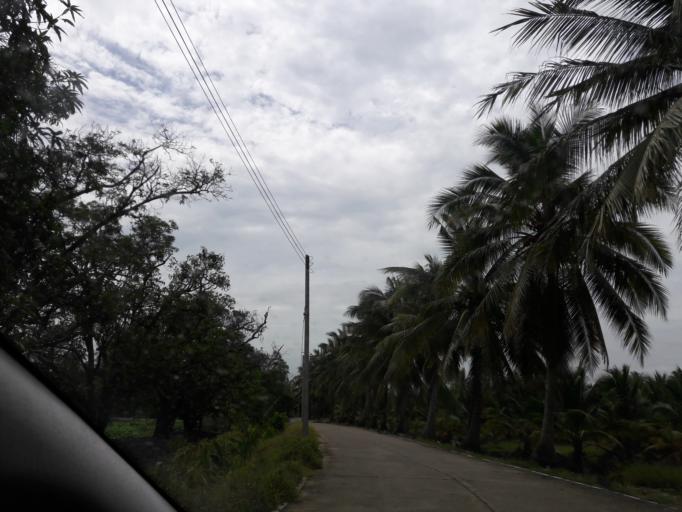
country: TH
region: Ratchaburi
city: Damnoen Saduak
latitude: 13.5227
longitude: 99.9541
